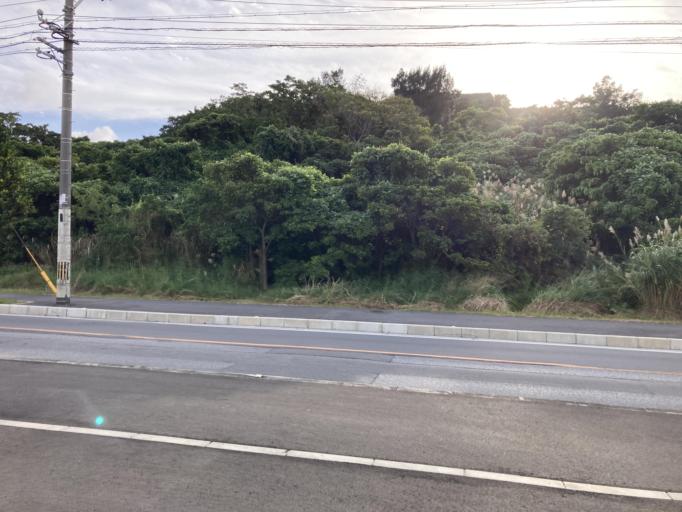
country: JP
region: Okinawa
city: Katsuren-haebaru
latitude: 26.3321
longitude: 127.8800
